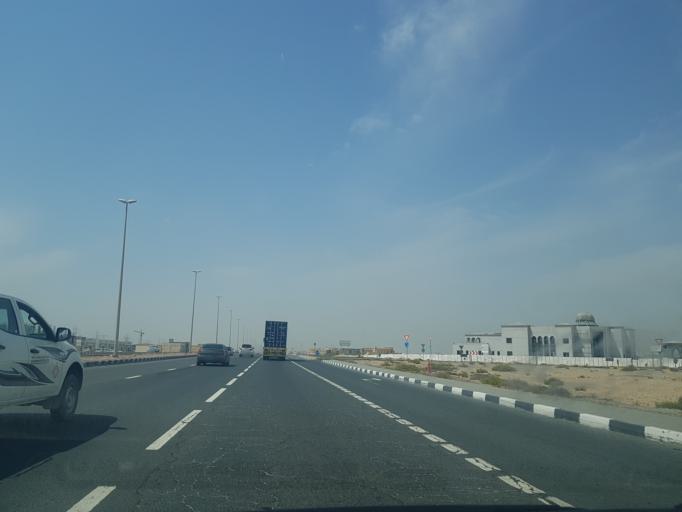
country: AE
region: Ash Shariqah
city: Sharjah
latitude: 25.2595
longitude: 55.5109
